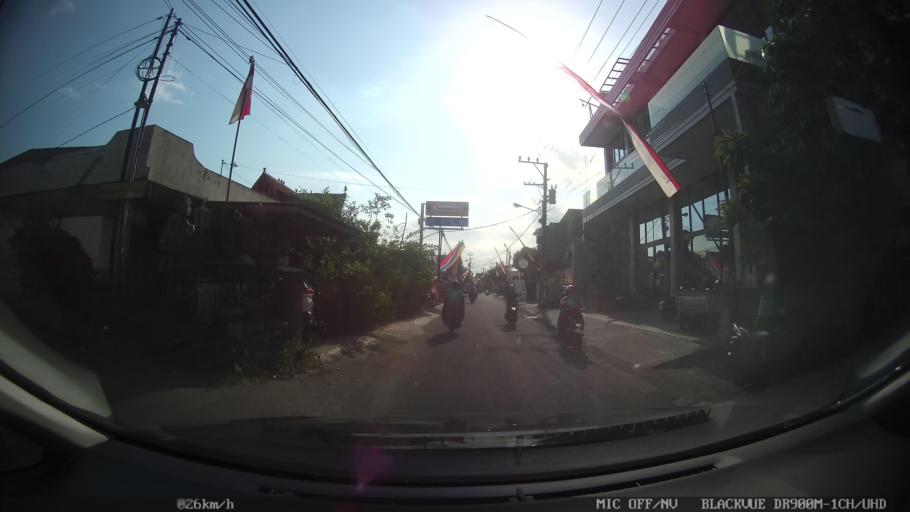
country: ID
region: Daerah Istimewa Yogyakarta
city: Yogyakarta
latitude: -7.7924
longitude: 110.3515
